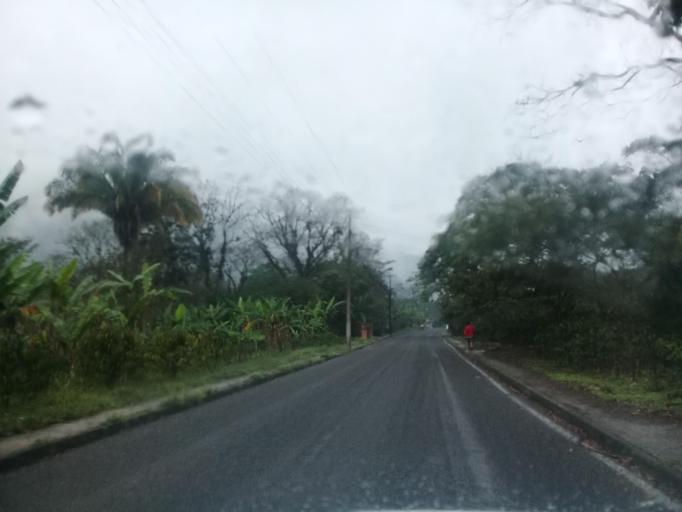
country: MX
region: Veracruz
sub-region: Amatlan de los Reyes
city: Centro de Readaptacion Social
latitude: 18.8009
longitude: -96.9464
